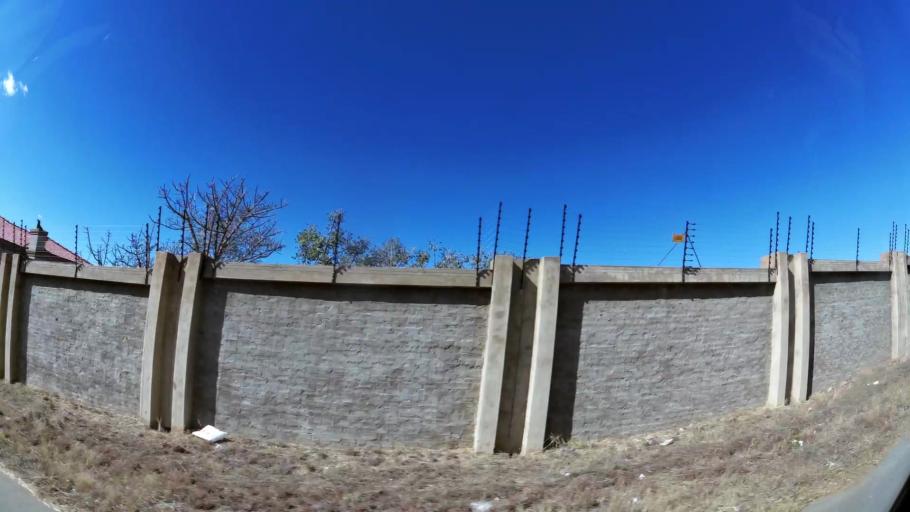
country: ZA
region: Limpopo
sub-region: Capricorn District Municipality
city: Polokwane
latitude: -23.8613
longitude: 29.5099
